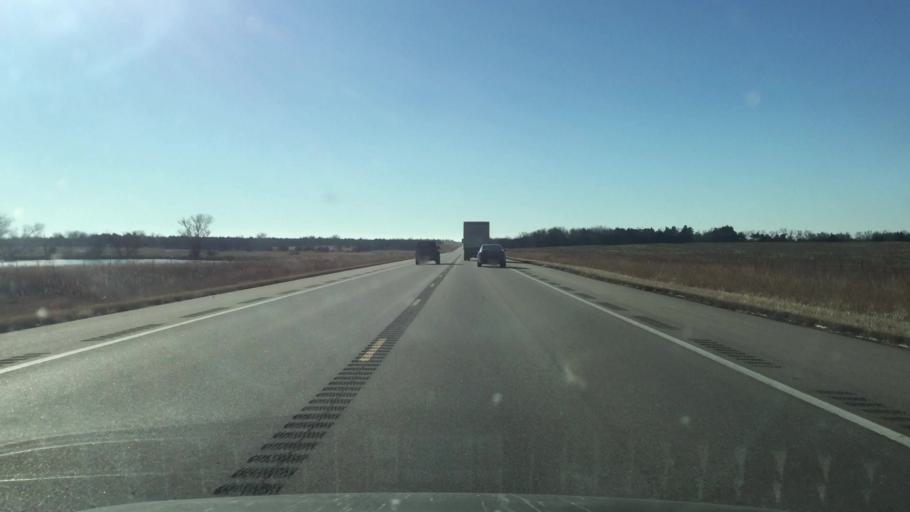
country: US
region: Kansas
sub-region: Allen County
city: Iola
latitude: 38.0447
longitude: -95.3805
